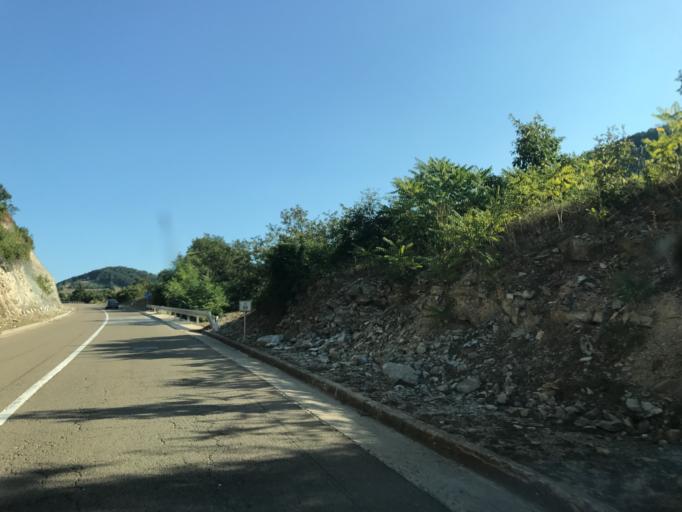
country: RO
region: Mehedinti
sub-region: Comuna Svinita
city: Svinita
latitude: 44.5380
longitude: 22.0317
